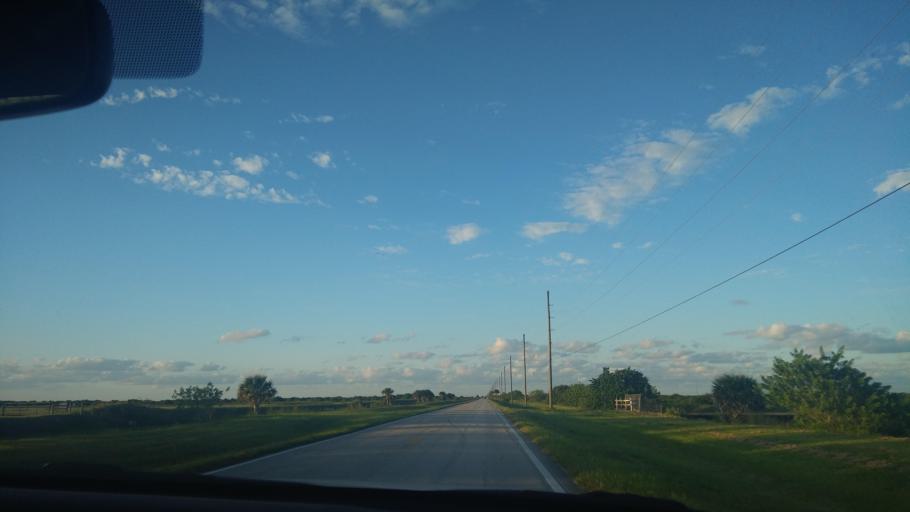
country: US
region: Florida
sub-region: Indian River County
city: Fellsmere
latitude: 27.7097
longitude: -80.6429
